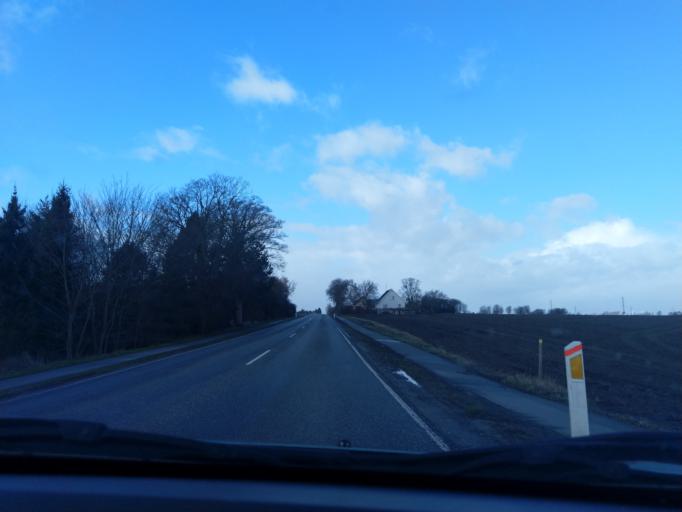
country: DK
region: Zealand
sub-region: Naestved Kommune
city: Naestved
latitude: 55.2719
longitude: 11.7350
